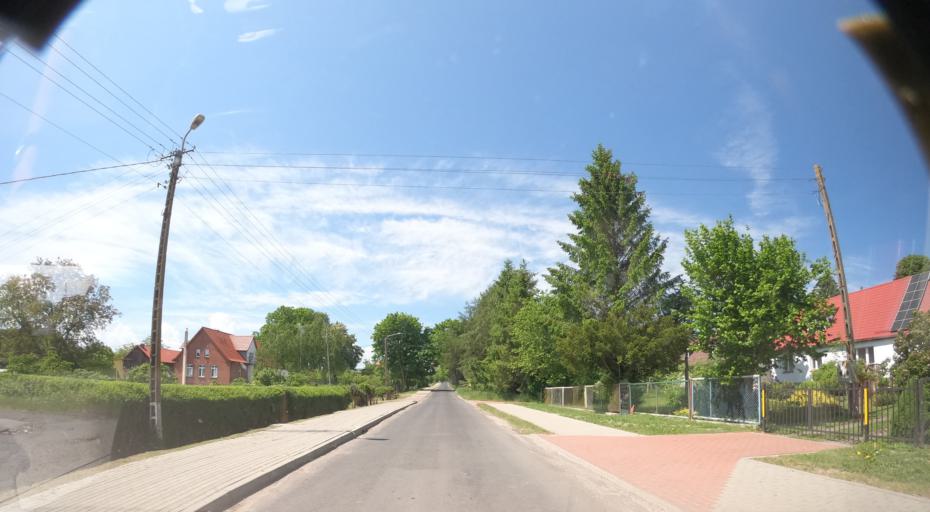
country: PL
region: West Pomeranian Voivodeship
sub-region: Powiat kolobrzeski
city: Dygowo
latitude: 54.1468
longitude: 15.7713
